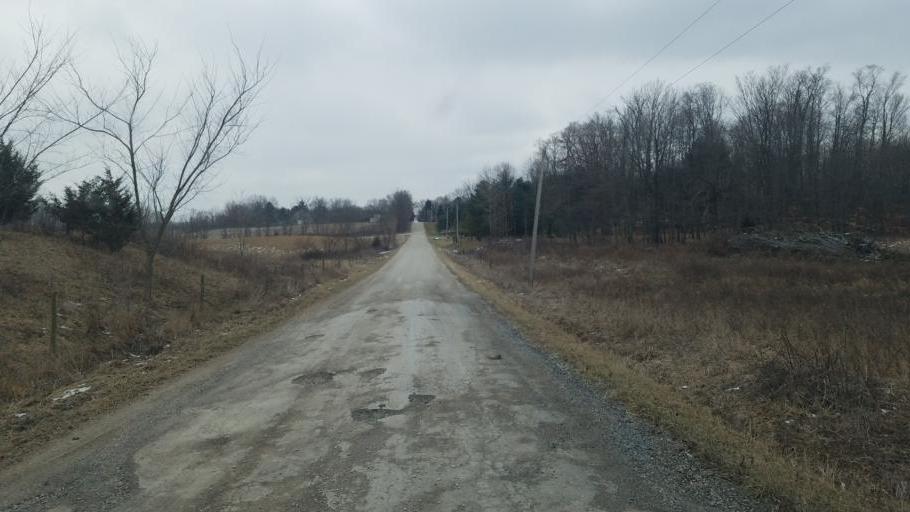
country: US
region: Ohio
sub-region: Morrow County
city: Mount Gilead
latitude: 40.5387
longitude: -82.7109
